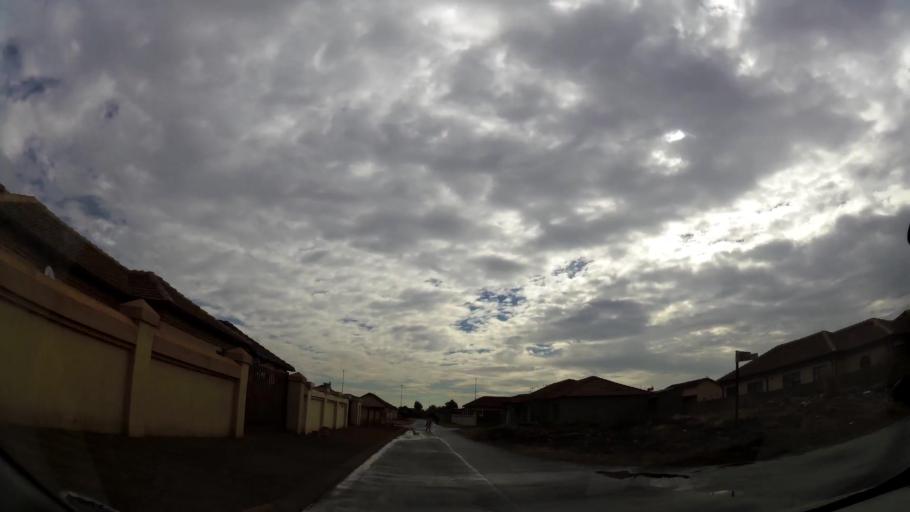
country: ZA
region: Gauteng
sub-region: Ekurhuleni Metropolitan Municipality
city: Germiston
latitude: -26.3319
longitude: 28.1923
